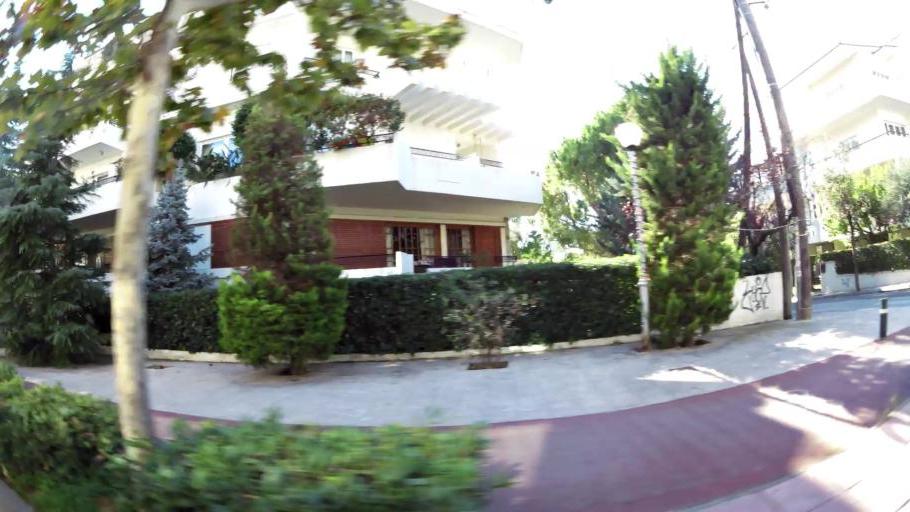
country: GR
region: Attica
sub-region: Nomarchia Athinas
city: Vrilissia
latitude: 38.0392
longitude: 23.8352
